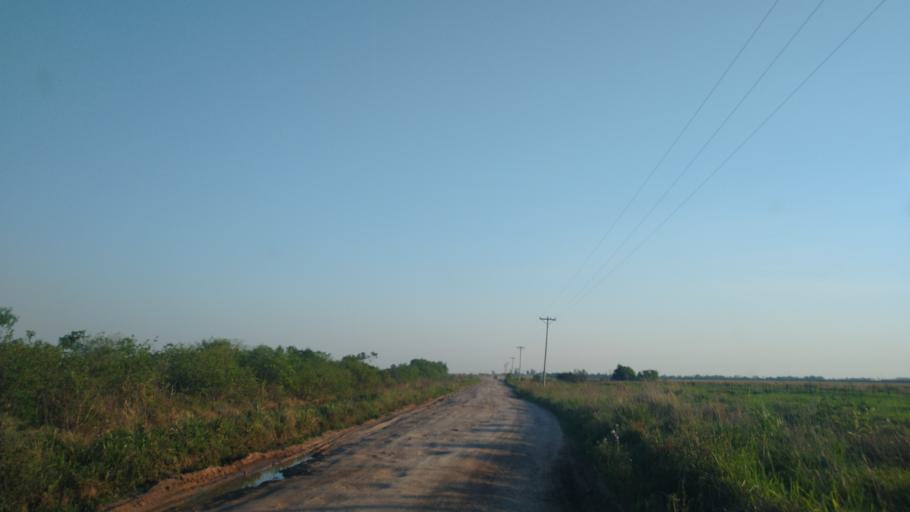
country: PY
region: Neembucu
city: Cerrito
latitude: -27.3924
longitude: -57.6588
